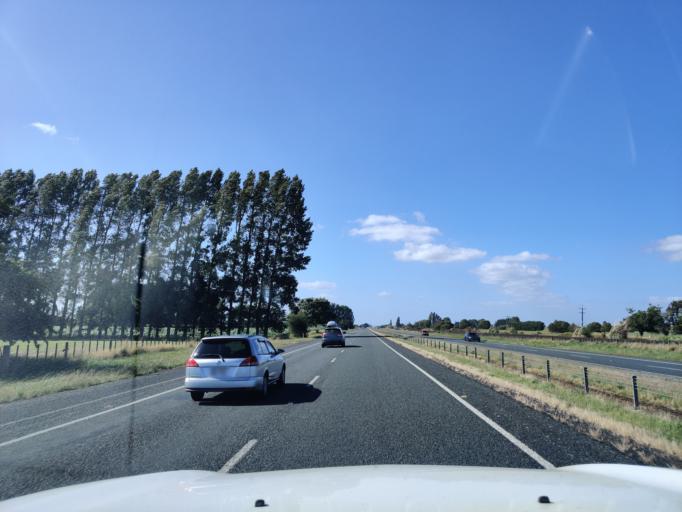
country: NZ
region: Waikato
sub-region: Waikato District
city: Te Kauwhata
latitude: -37.4797
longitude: 175.1599
